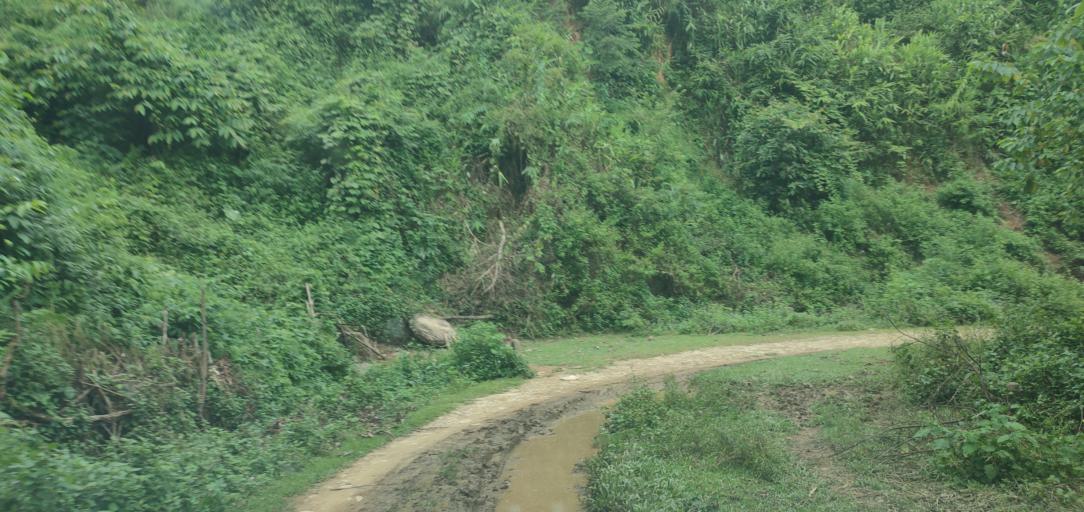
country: LA
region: Phongsali
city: Phongsali
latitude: 21.4415
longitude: 102.3188
